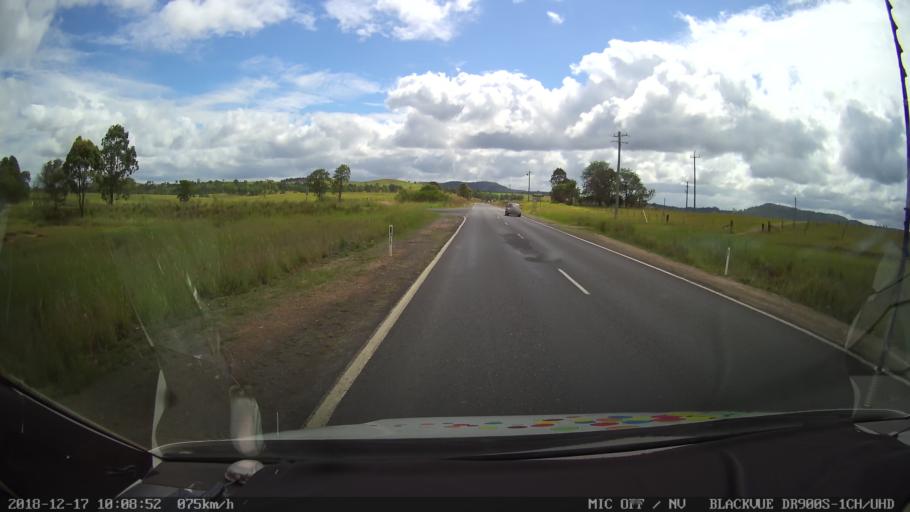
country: AU
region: New South Wales
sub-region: Tenterfield Municipality
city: Carrolls Creek
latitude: -28.8894
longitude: 152.5369
